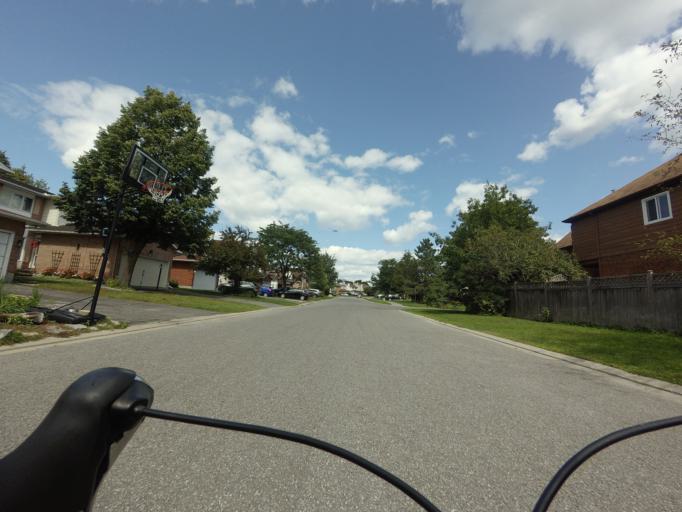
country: CA
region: Ontario
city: Bells Corners
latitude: 45.2992
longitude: -75.8620
